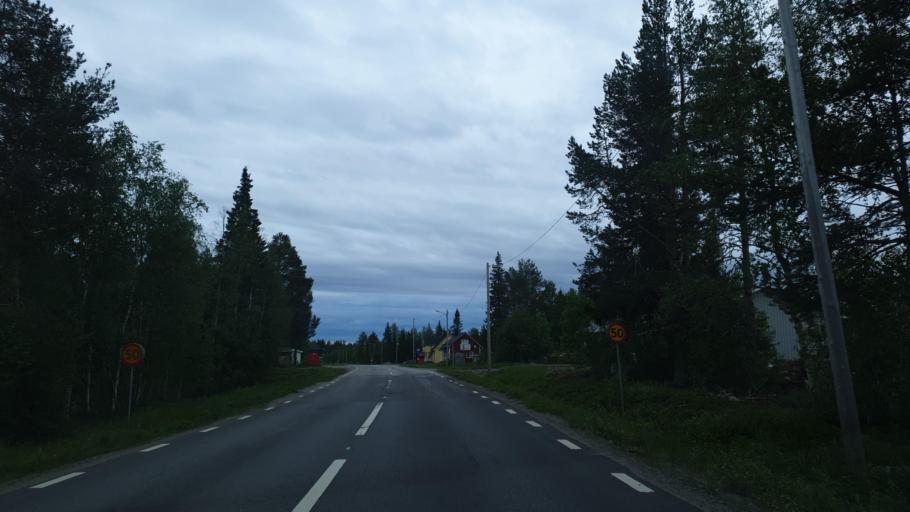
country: SE
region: Norrbotten
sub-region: Jokkmokks Kommun
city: Jokkmokk
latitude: 66.1557
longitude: 19.9804
